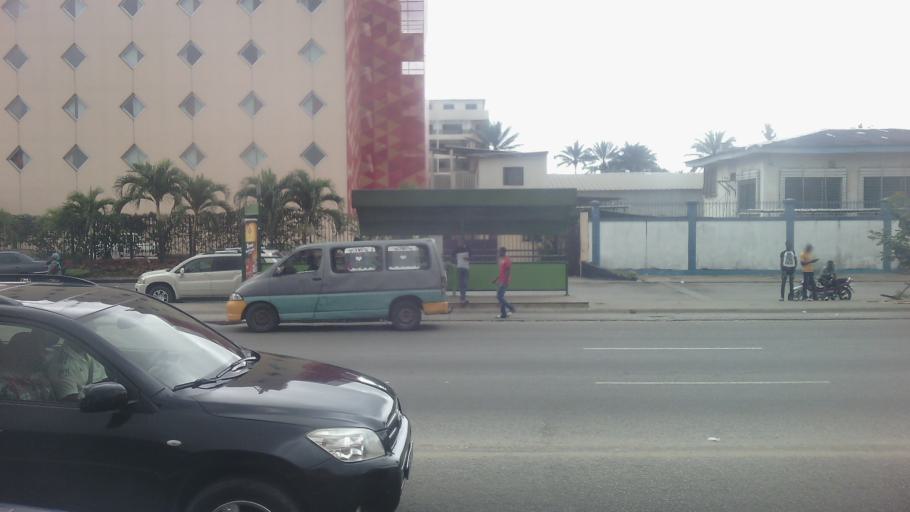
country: CI
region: Lagunes
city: Abidjan
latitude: 5.2919
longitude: -3.9736
